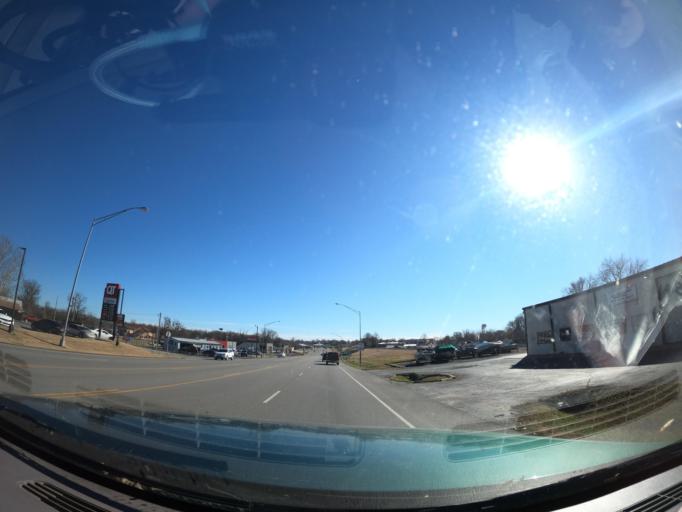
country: US
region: Oklahoma
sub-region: Wagoner County
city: Coweta
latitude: 35.9582
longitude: -95.6512
